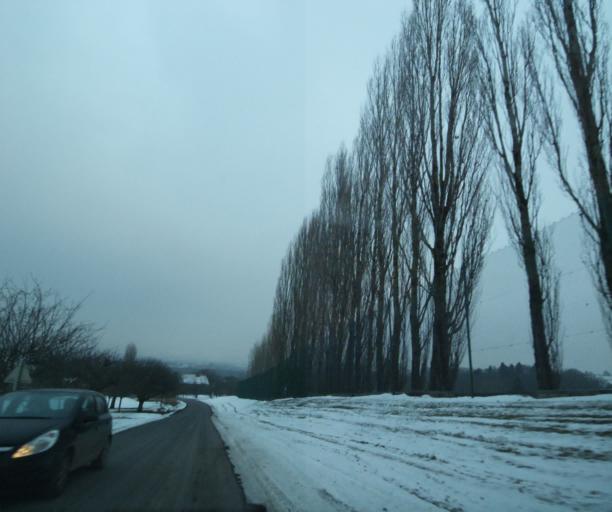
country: FR
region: Rhone-Alpes
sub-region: Departement de la Haute-Savoie
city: Reignier-Esery
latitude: 46.1428
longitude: 6.2430
